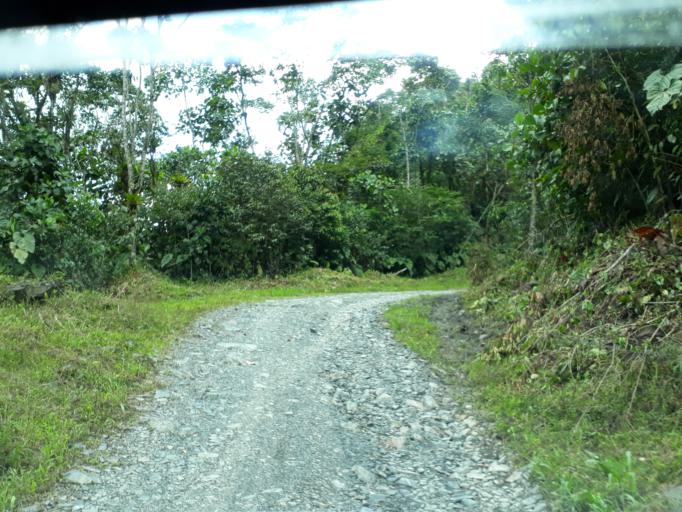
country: CO
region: Cundinamarca
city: Topaipi
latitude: 5.3092
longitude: -74.2039
